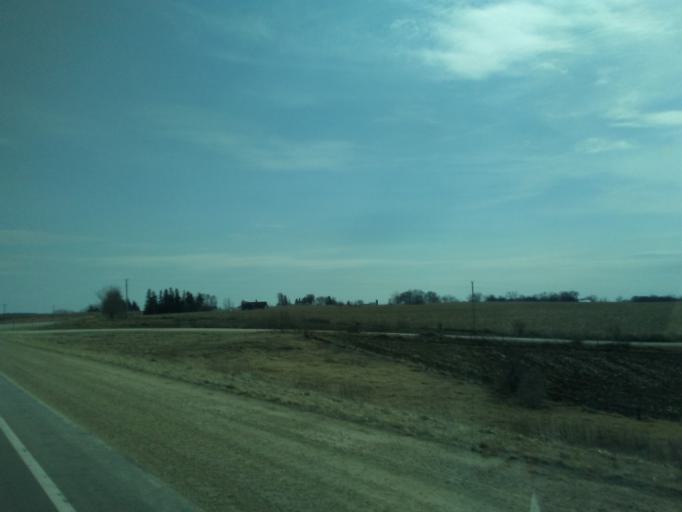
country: US
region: Iowa
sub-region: Winneshiek County
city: Decorah
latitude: 43.4515
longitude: -91.8656
